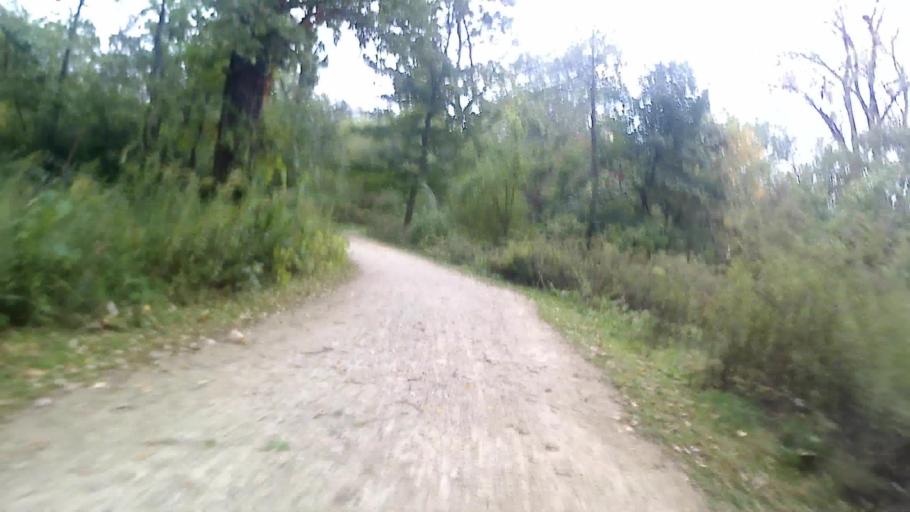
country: US
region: Illinois
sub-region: DuPage County
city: Warrenville
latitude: 41.8220
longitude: -88.1718
